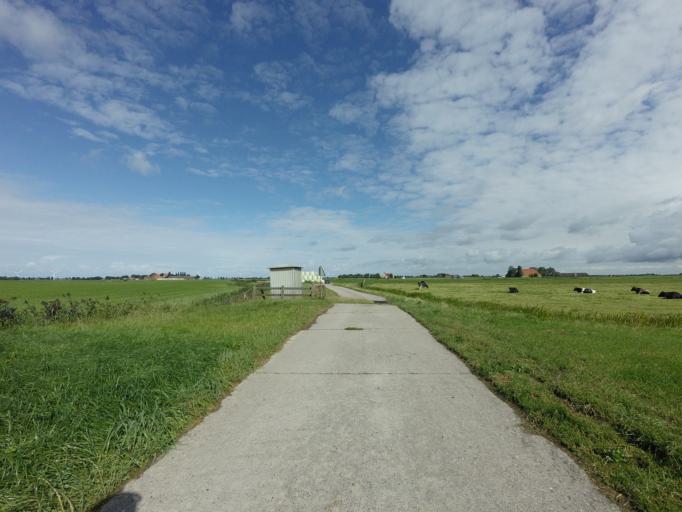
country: NL
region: Friesland
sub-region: Sudwest Fryslan
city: Workum
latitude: 53.0388
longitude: 5.4612
